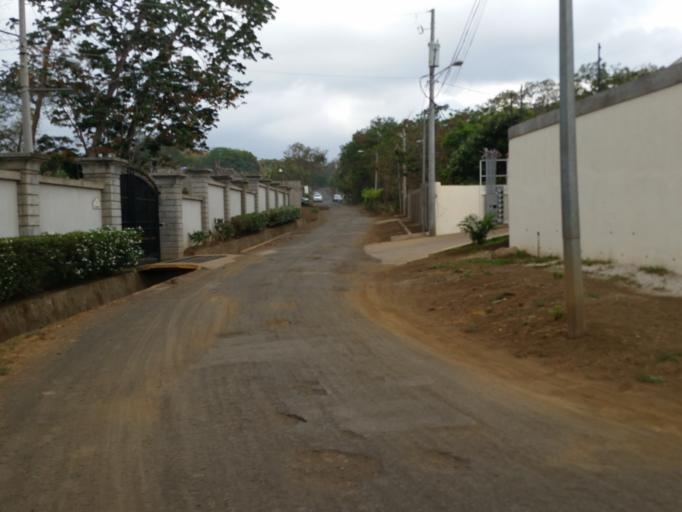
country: NI
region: Managua
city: Managua
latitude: 12.0758
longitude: -86.2531
